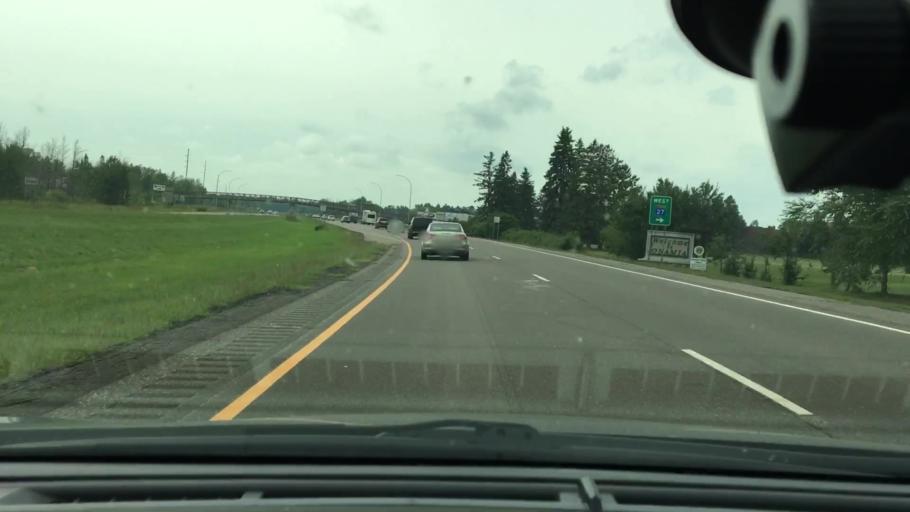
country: US
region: Minnesota
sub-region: Mille Lacs County
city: Vineland
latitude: 46.0755
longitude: -93.6564
